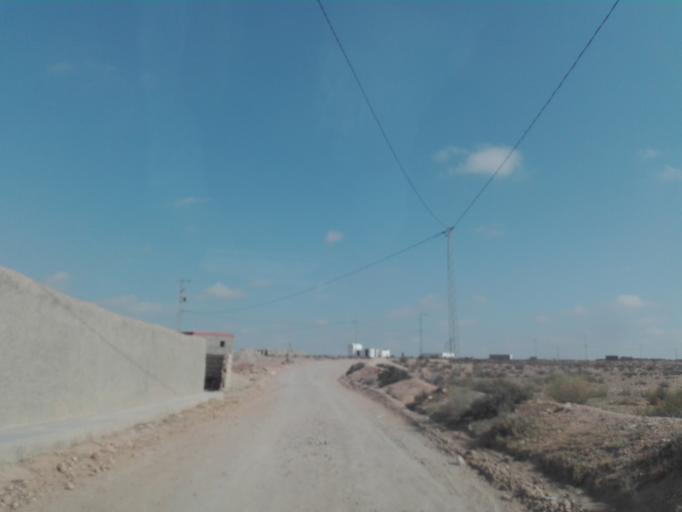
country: TN
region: Madanin
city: Medenine
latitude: 33.4280
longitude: 10.4058
